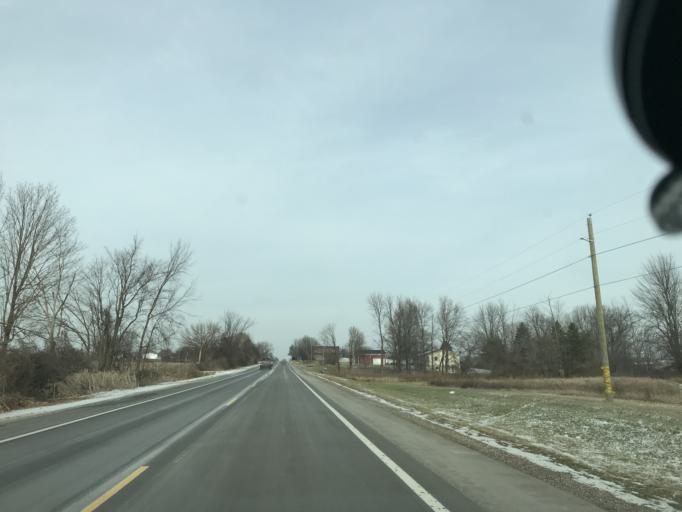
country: US
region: Michigan
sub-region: Ionia County
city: Lake Odessa
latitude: 42.7772
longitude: -85.0743
